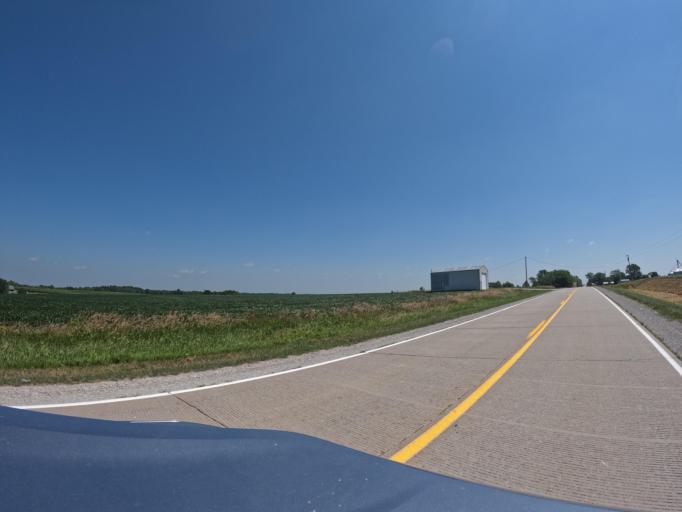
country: US
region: Iowa
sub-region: Keokuk County
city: Sigourney
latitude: 41.2648
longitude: -92.2556
